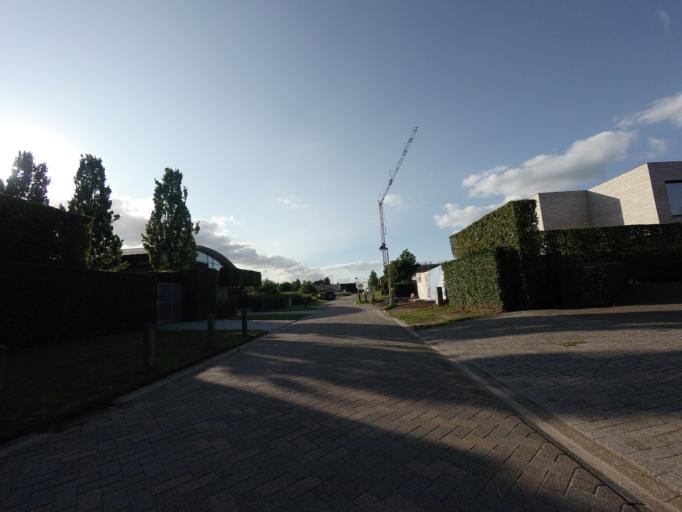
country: BE
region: Flanders
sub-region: Provincie Antwerpen
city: Edegem
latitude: 51.1492
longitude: 4.4405
